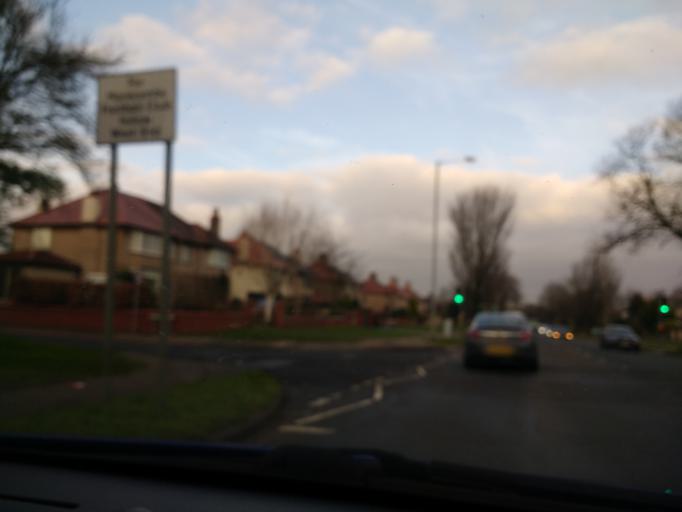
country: GB
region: England
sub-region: Lancashire
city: Morecambe
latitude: 54.0649
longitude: -2.8356
